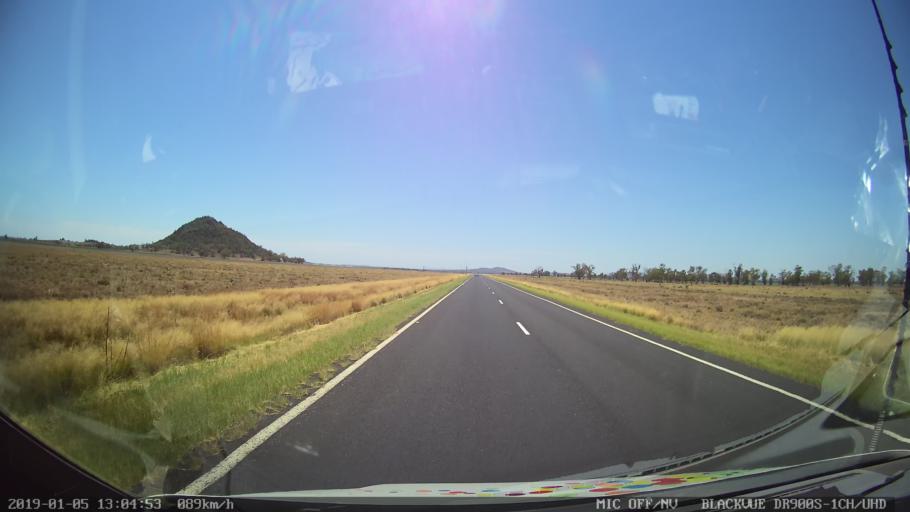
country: AU
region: New South Wales
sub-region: Gunnedah
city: Gunnedah
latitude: -31.0996
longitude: 149.8459
